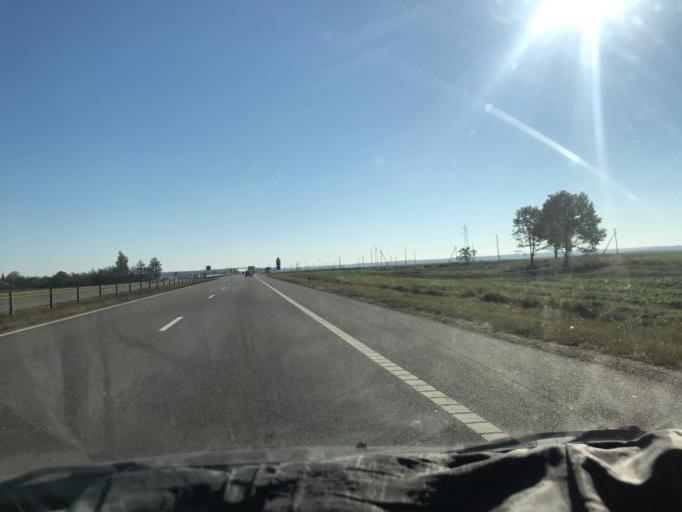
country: BY
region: Mogilev
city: Yalizava
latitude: 53.2360
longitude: 28.9712
